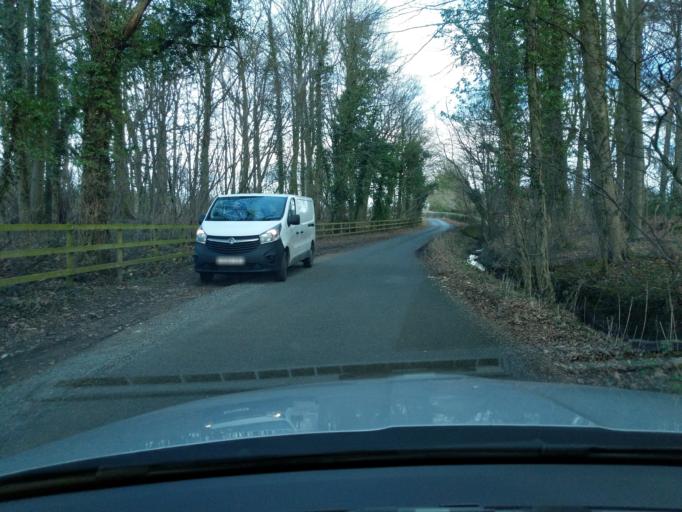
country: GB
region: England
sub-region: North Yorkshire
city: Catterick
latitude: 54.3740
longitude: -1.6737
